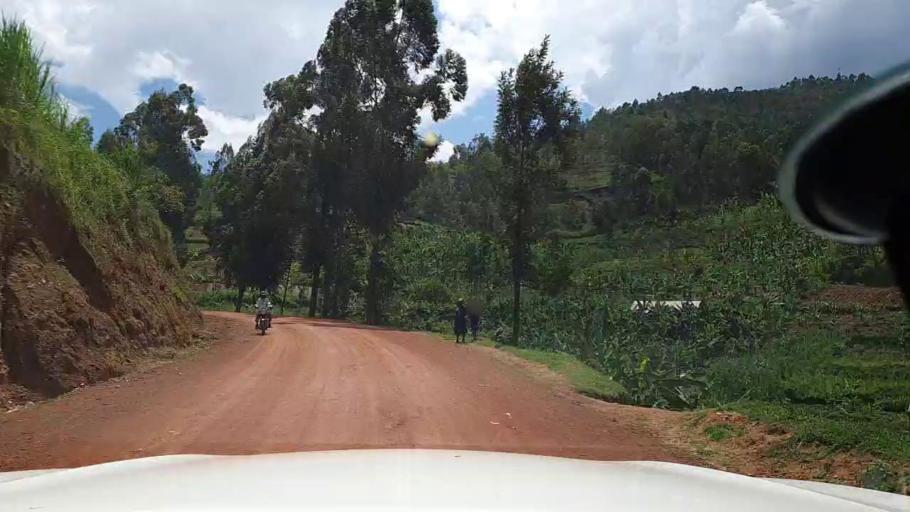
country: RW
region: Northern Province
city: Byumba
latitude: -1.7531
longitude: 29.8502
